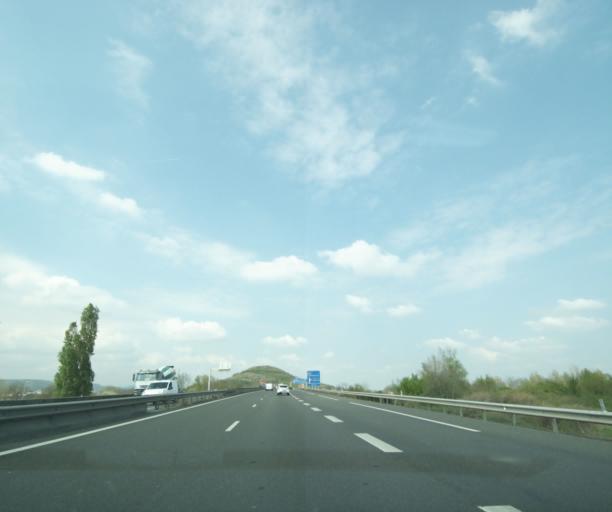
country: FR
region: Auvergne
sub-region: Departement du Puy-de-Dome
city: Perignat-les-Sarlieve
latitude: 45.7623
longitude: 3.1392
